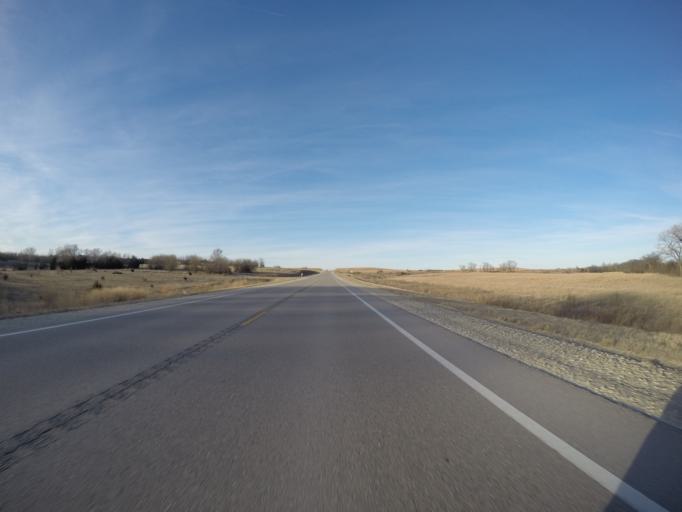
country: US
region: Kansas
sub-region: Marion County
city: Marion
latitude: 38.2774
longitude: -96.9624
